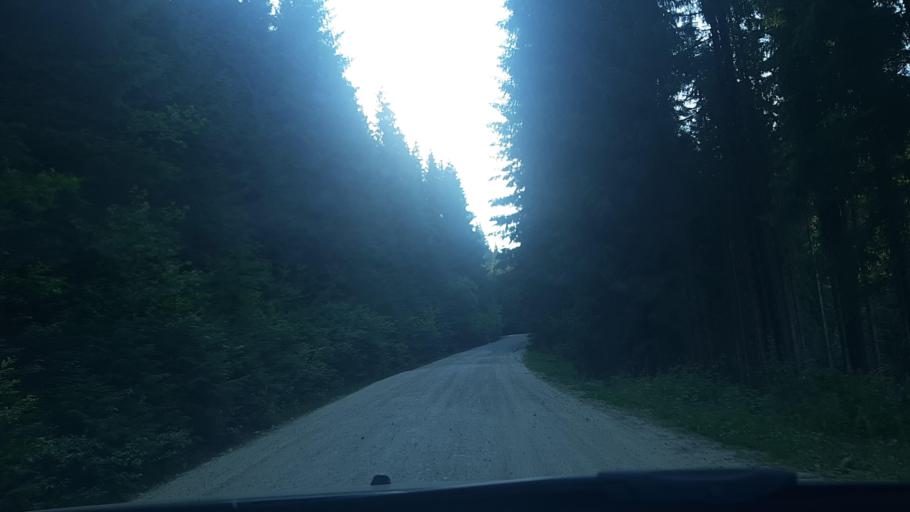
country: RO
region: Alba
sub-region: Comuna Sugag
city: Sugag
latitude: 45.5759
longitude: 23.6079
